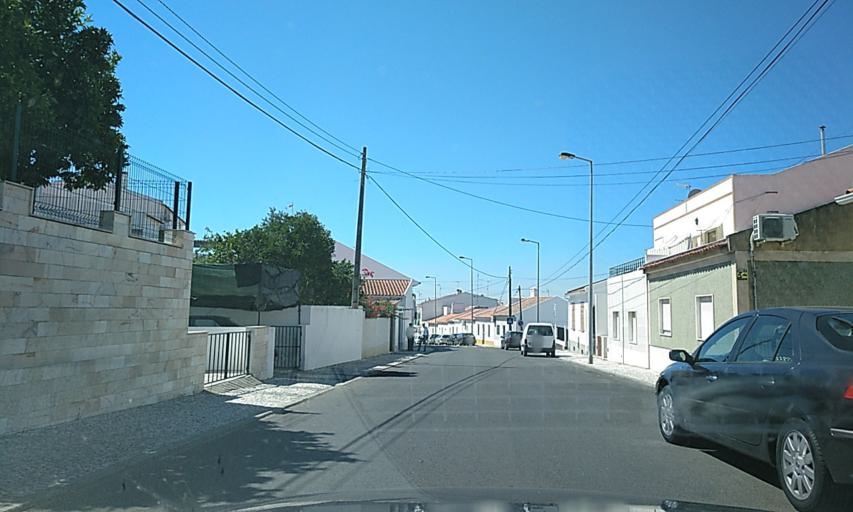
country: PT
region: Portalegre
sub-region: Campo Maior
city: Campo Maior
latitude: 39.0185
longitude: -7.0683
